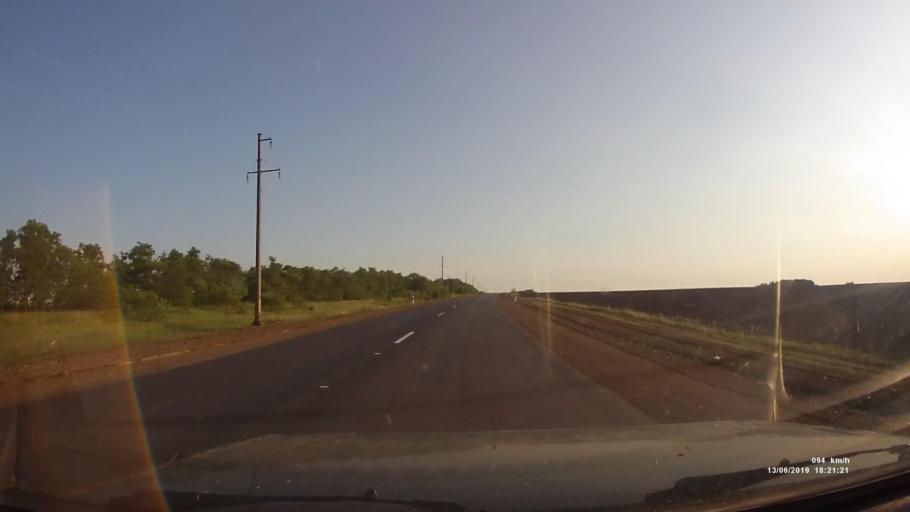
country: RU
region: Rostov
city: Kazanskaya
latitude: 49.8716
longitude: 41.2921
